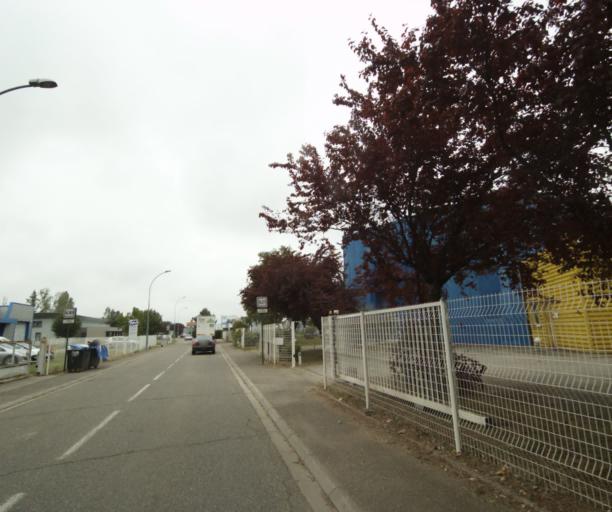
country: FR
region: Midi-Pyrenees
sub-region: Departement du Tarn-et-Garonne
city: Bressols
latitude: 43.9942
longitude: 1.3342
